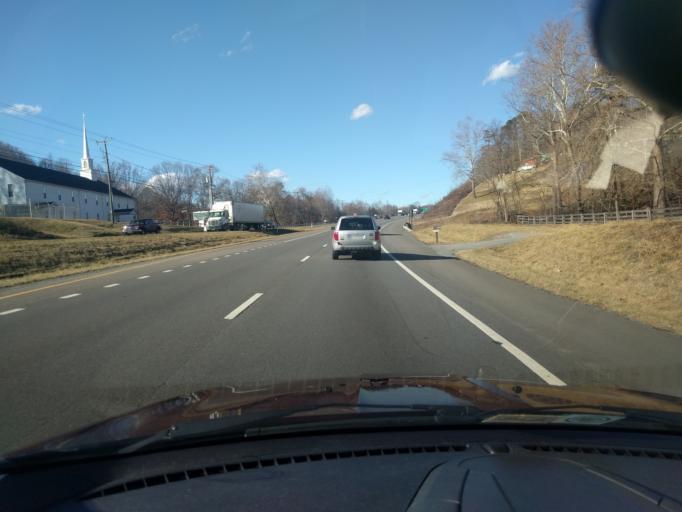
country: US
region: Virginia
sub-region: Botetourt County
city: Cloverdale
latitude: 37.3446
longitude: -79.8814
